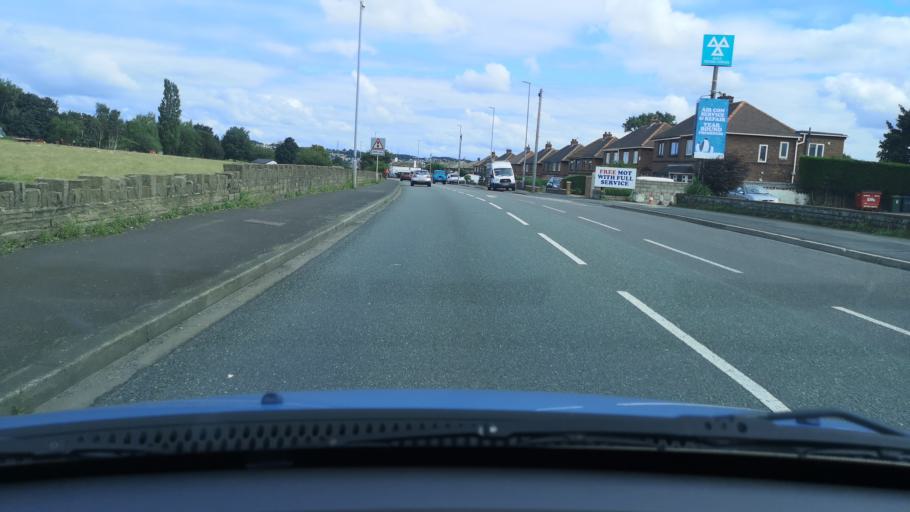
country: GB
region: England
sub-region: Kirklees
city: Heckmondwike
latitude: 53.7206
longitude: -1.6701
